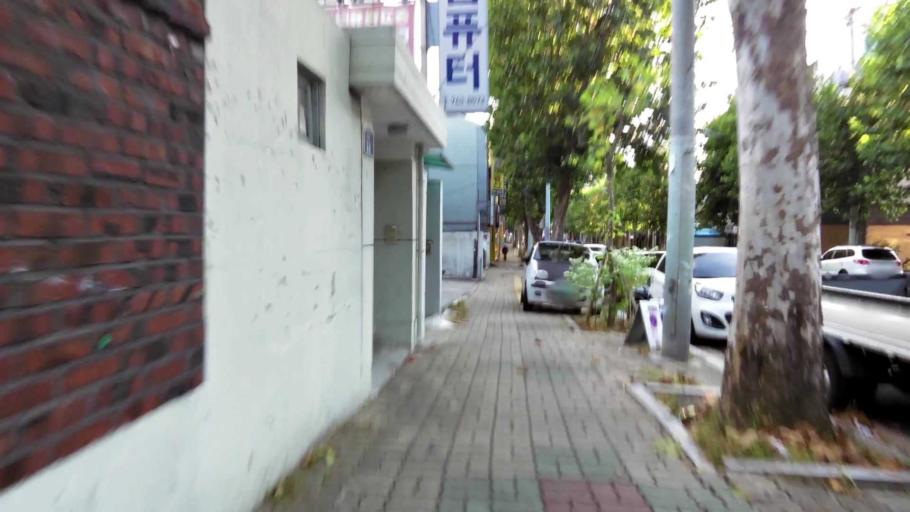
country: KR
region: Daegu
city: Daegu
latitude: 35.8611
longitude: 128.6400
